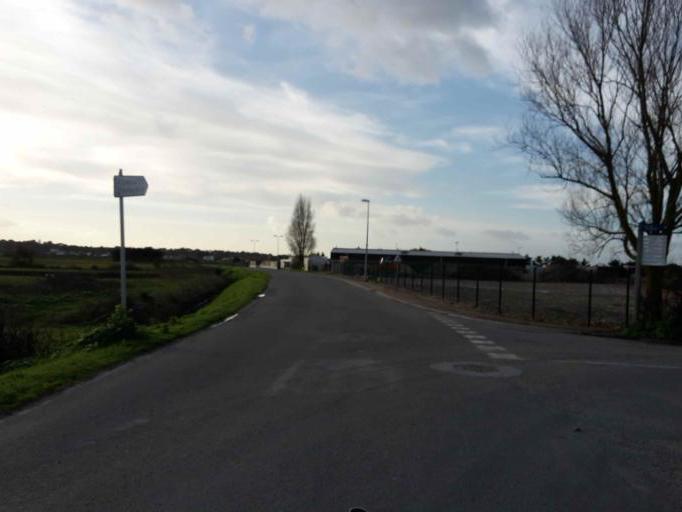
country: FR
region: Pays de la Loire
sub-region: Departement de la Vendee
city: La Gueriniere
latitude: 46.9720
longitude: -2.2490
